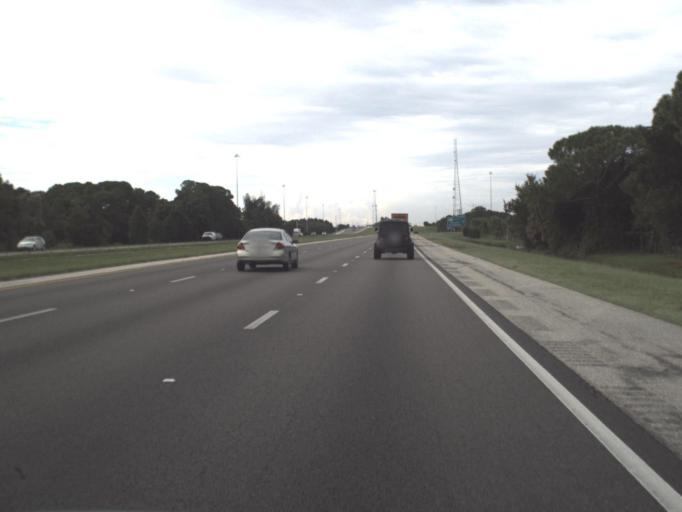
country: US
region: Florida
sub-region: Sarasota County
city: Fruitville
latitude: 27.3476
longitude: -82.4468
